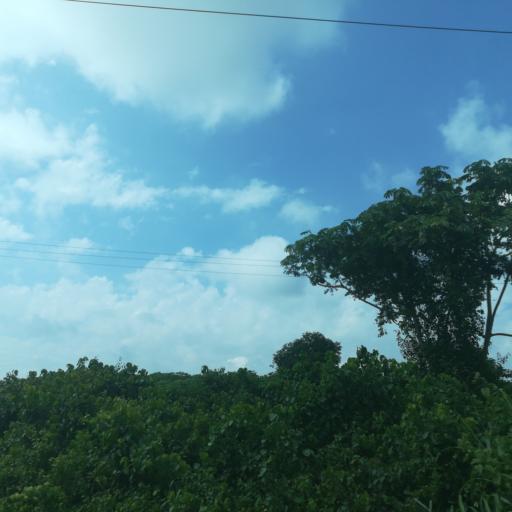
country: NG
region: Lagos
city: Ikorodu
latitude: 6.6718
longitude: 3.6628
